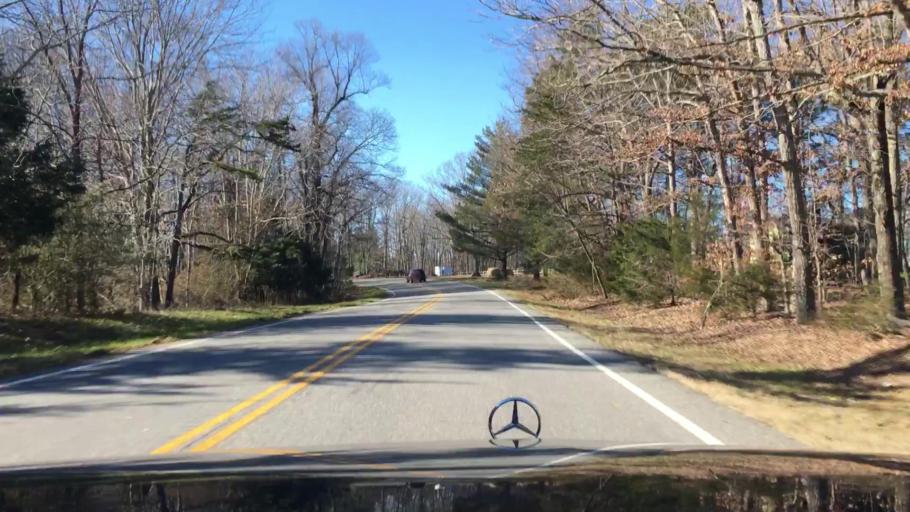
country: US
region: Virginia
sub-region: City of Bedford
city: Bedford
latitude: 37.2223
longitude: -79.5095
